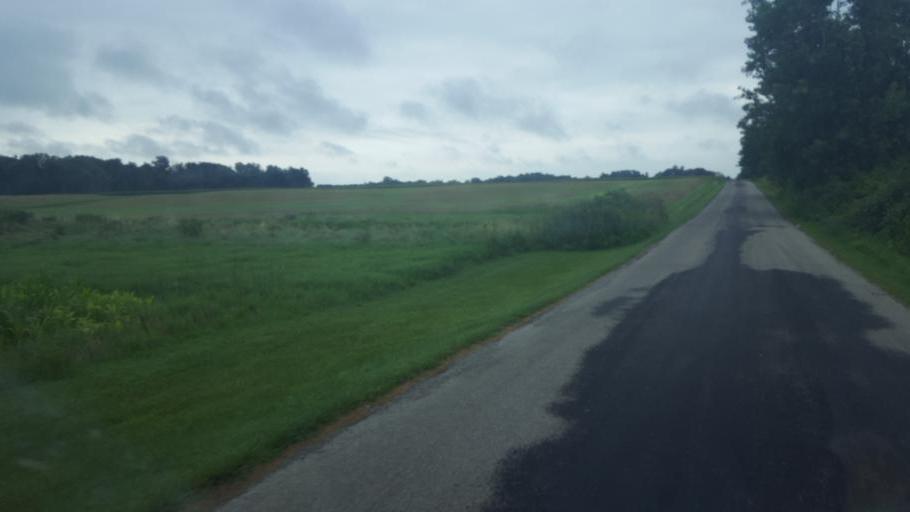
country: US
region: Ohio
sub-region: Knox County
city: Centerburg
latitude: 40.4000
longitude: -82.7405
